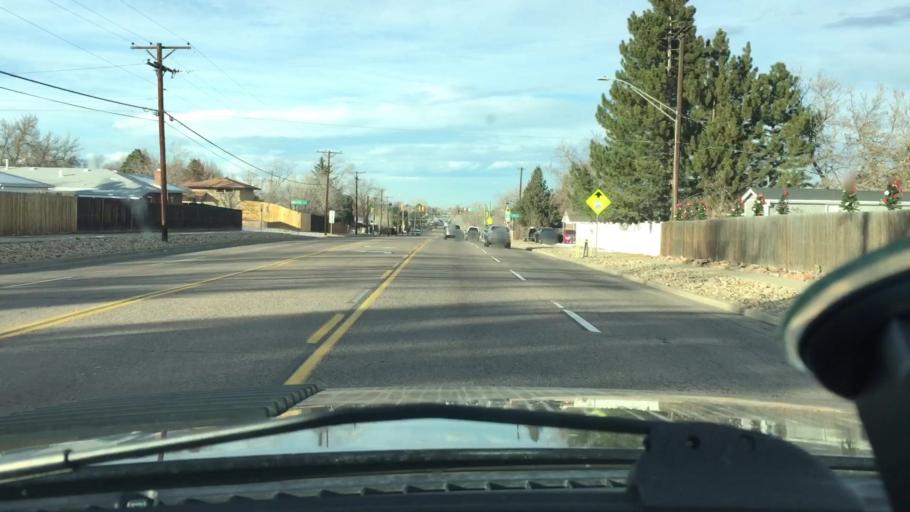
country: US
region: Colorado
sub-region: Adams County
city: Northglenn
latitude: 39.8768
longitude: -104.9967
